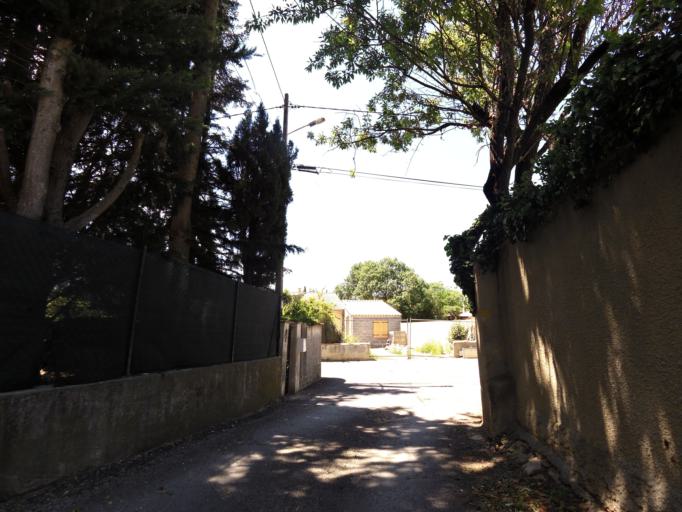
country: FR
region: Languedoc-Roussillon
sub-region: Departement du Gard
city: Aigues-Vives
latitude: 43.7370
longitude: 4.1714
